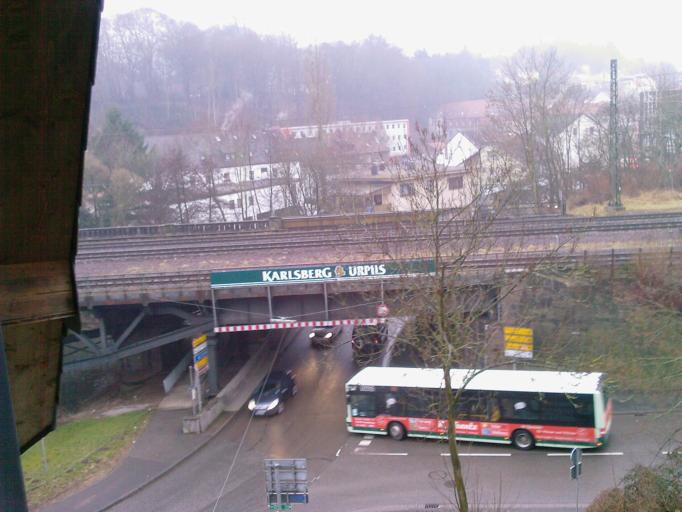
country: DE
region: Saarland
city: Ottweiler
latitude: 49.4008
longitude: 7.1667
